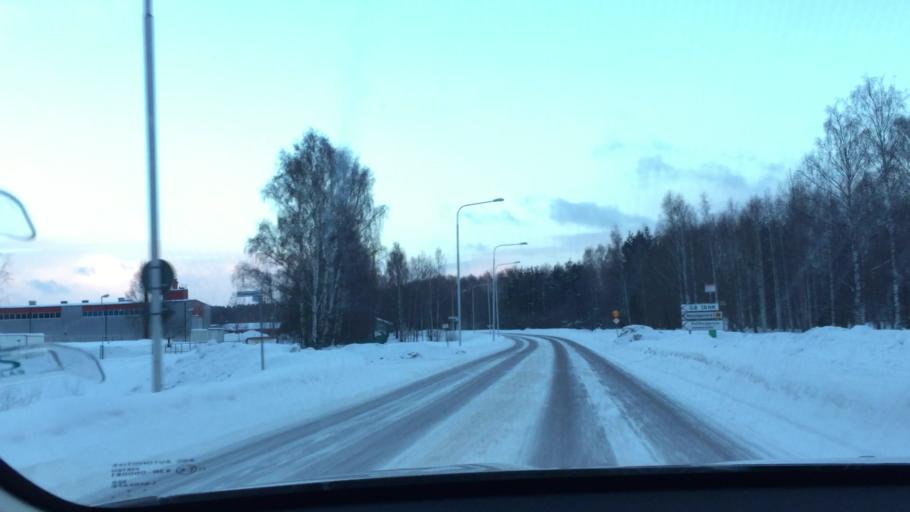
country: SE
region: Dalarna
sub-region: Faluns Kommun
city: Falun
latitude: 60.5844
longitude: 15.6538
